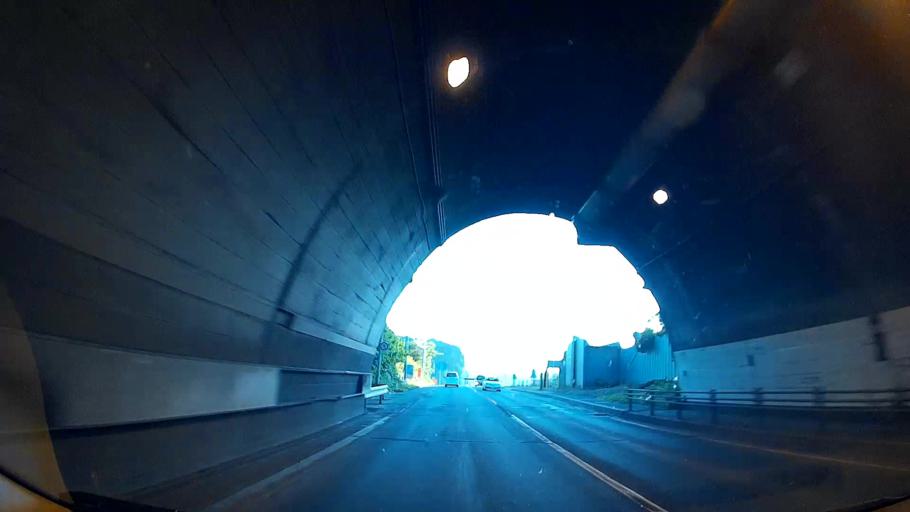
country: JP
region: Hokkaido
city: Otaru
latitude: 43.2092
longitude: 140.8995
